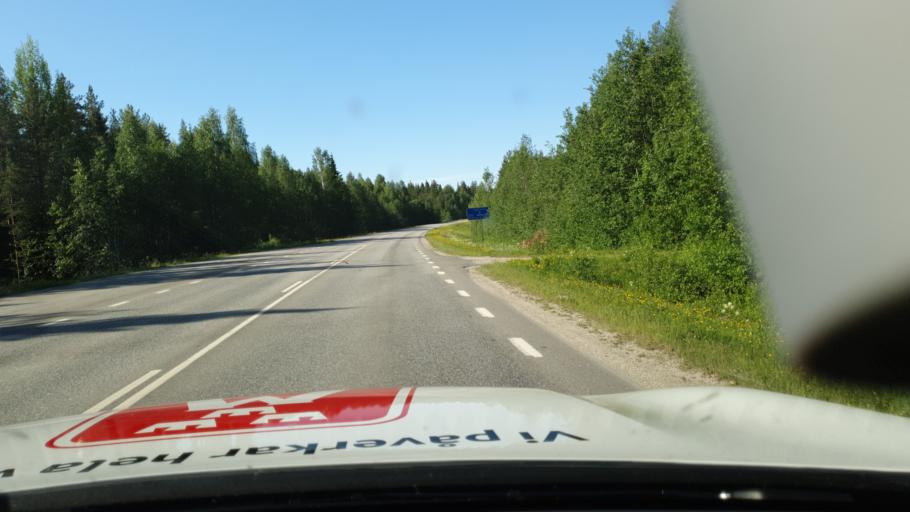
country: SE
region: Vaesterbotten
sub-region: Lycksele Kommun
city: Lycksele
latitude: 64.5801
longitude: 18.6577
